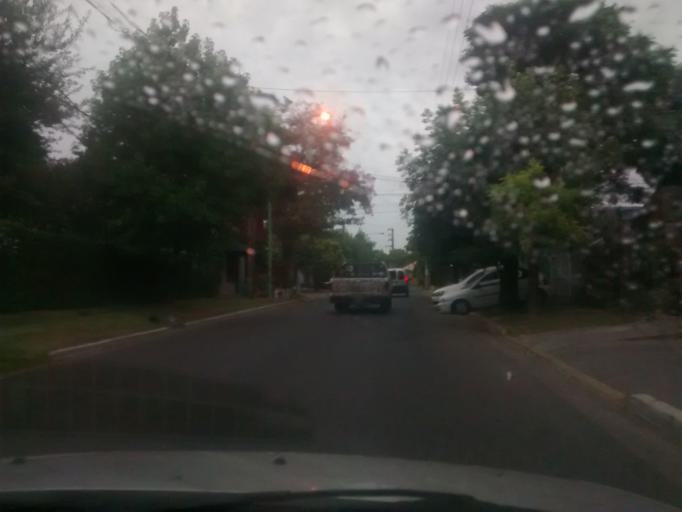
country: AR
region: Buenos Aires
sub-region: Partido de La Plata
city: La Plata
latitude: -34.8952
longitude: -58.0241
